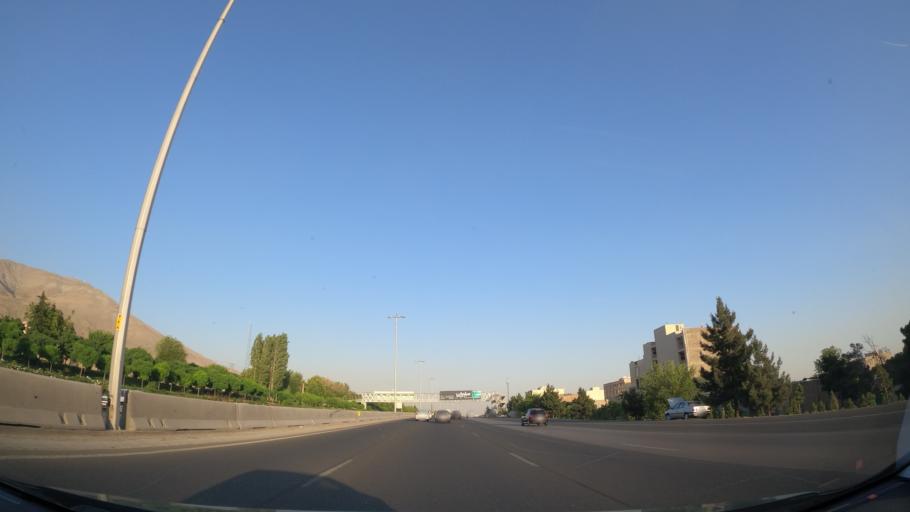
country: IR
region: Alborz
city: Karaj
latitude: 35.7837
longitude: 51.0295
